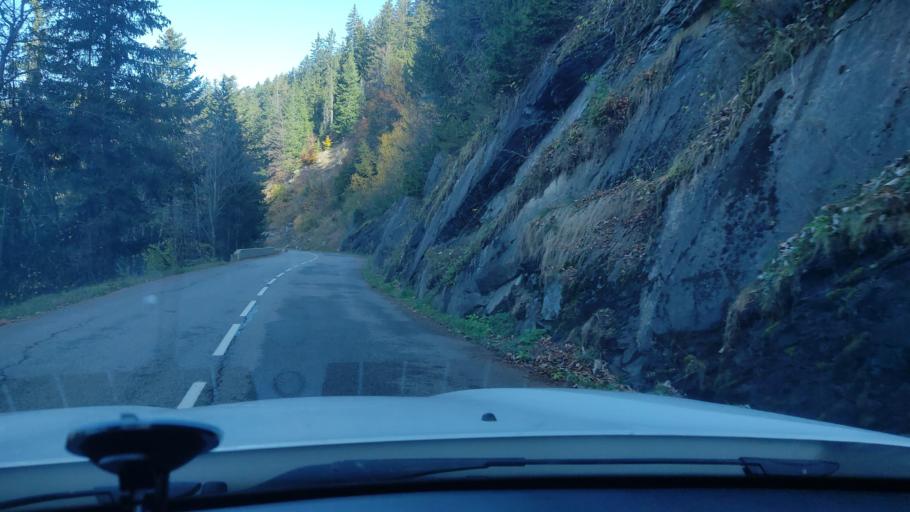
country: FR
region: Rhone-Alpes
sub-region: Departement de la Savoie
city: Villargondran
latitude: 45.2235
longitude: 6.3334
